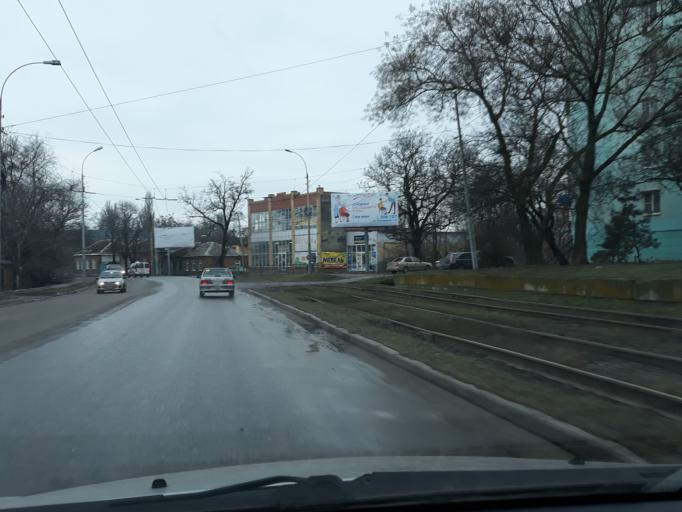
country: RU
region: Rostov
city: Taganrog
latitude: 47.2273
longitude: 38.9174
